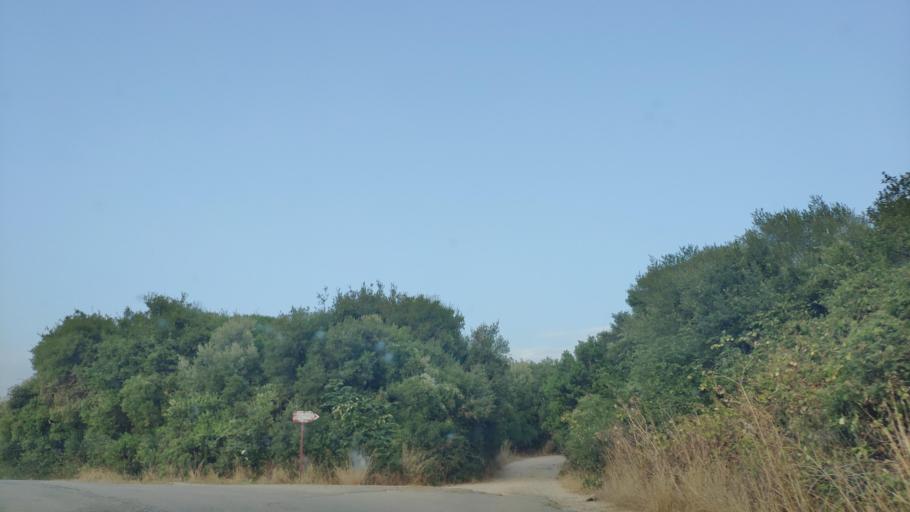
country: GR
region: West Greece
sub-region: Nomos Aitolias kai Akarnanias
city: Monastirakion
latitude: 38.9165
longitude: 20.9748
